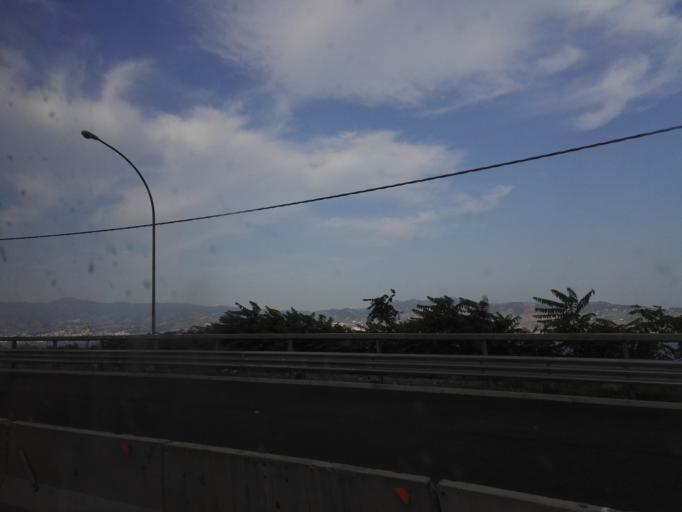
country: IT
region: Calabria
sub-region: Provincia di Reggio Calabria
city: Campo Calabro
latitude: 38.2272
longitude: 15.6457
